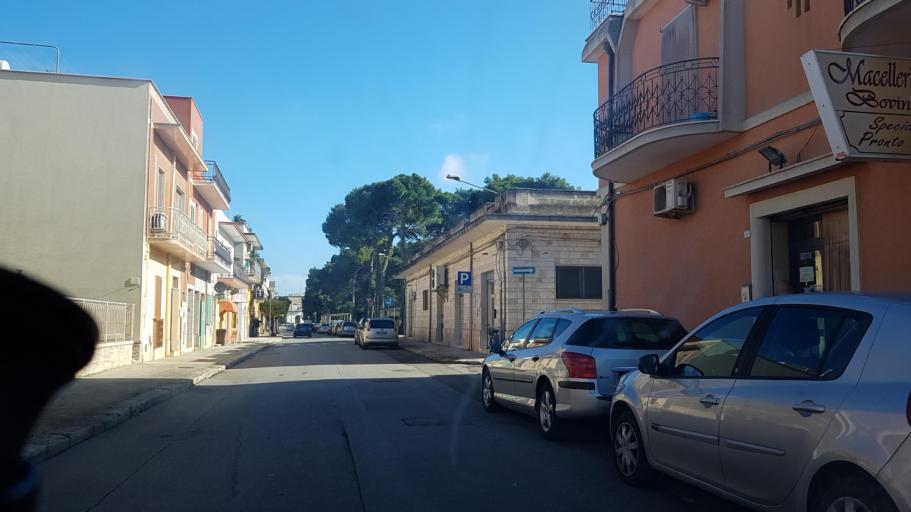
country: IT
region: Apulia
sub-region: Provincia di Brindisi
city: San Vito dei Normanni
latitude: 40.6565
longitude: 17.6988
